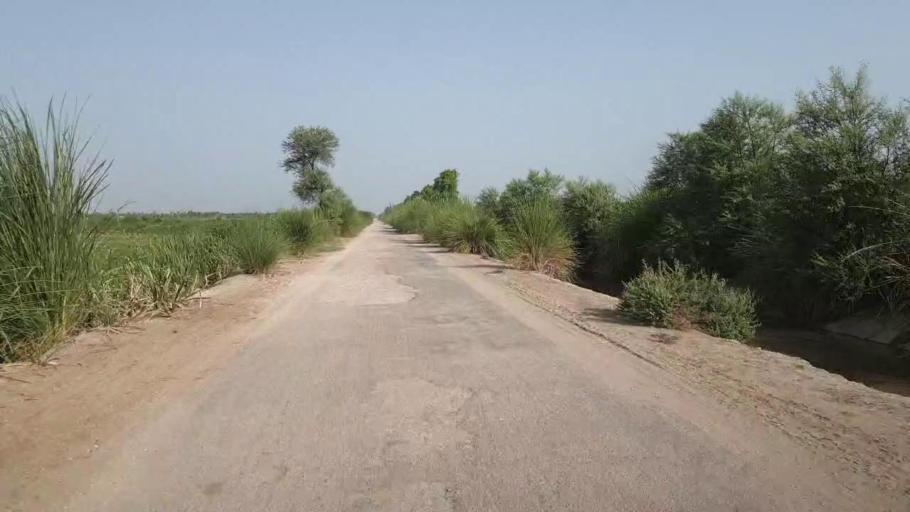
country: PK
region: Sindh
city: Daur
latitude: 26.3464
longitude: 68.1772
